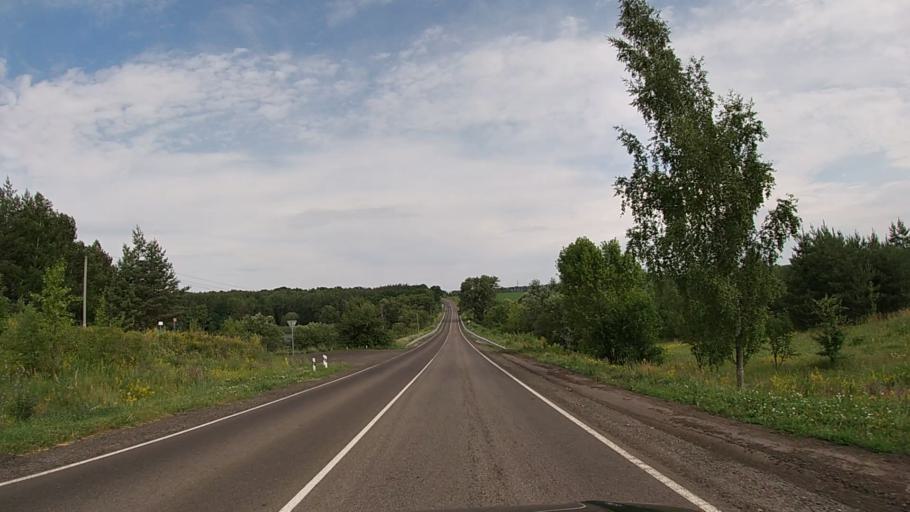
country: RU
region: Belgorod
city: Krasnaya Yaruga
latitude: 50.8260
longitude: 35.4982
